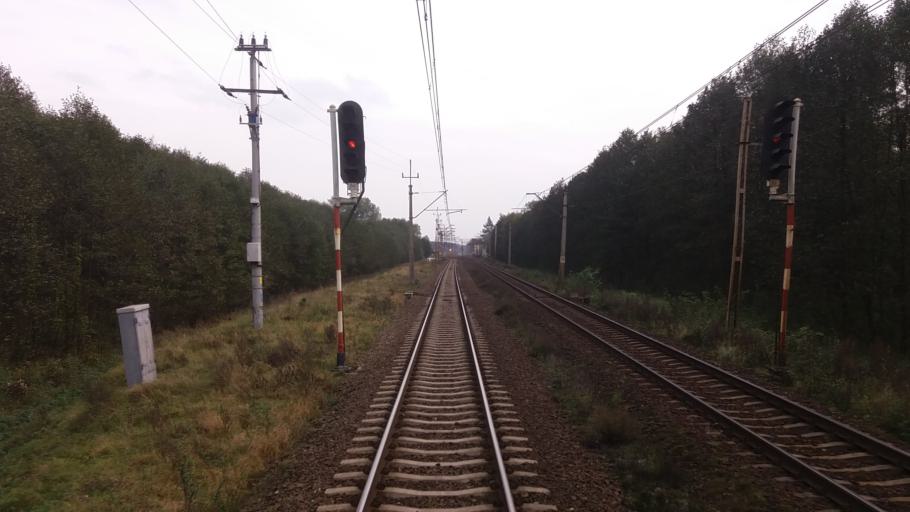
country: PL
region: West Pomeranian Voivodeship
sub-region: Powiat stargardzki
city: Kobylanka
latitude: 53.3735
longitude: 14.8542
